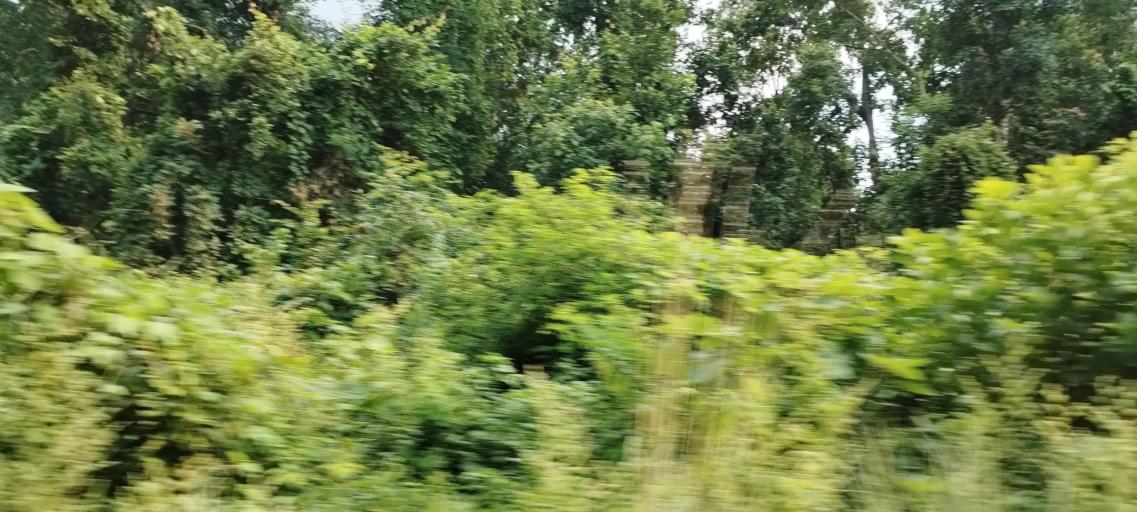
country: NP
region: Mid Western
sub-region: Bheri Zone
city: Bardiya
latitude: 28.4301
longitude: 81.3509
